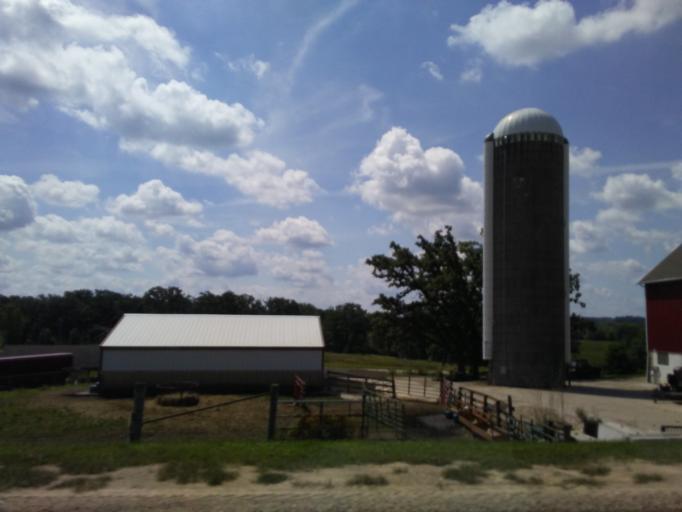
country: US
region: Wisconsin
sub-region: Dane County
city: Verona
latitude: 42.9879
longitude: -89.5660
